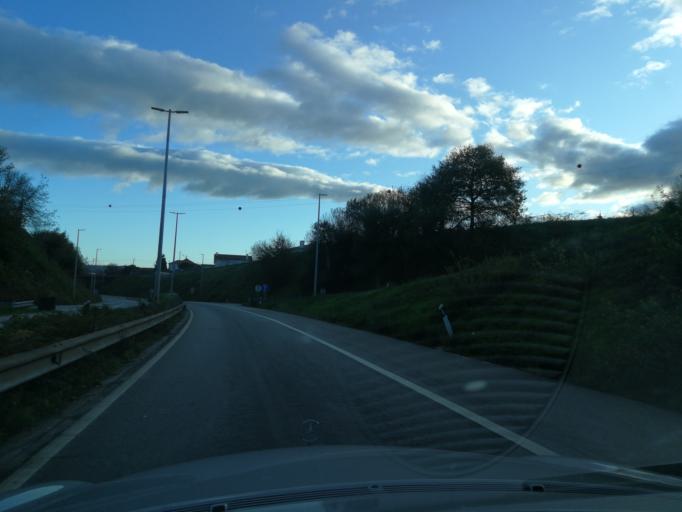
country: PT
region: Braga
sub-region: Barcelos
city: Vila Frescainha
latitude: 41.5313
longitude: -8.6400
